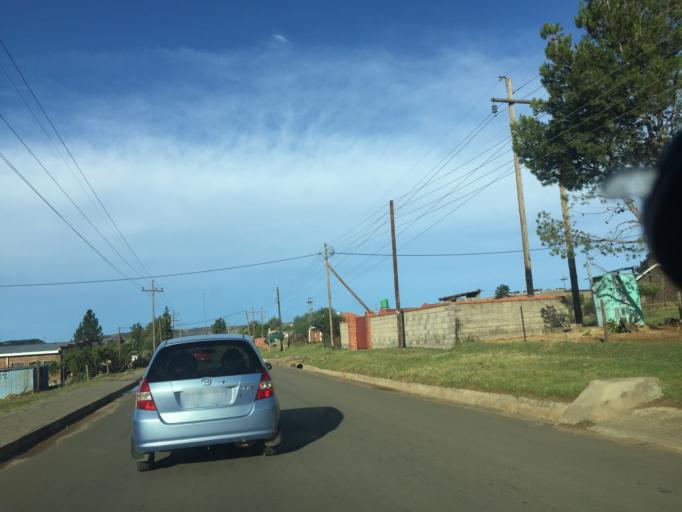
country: LS
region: Maseru
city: Maseru
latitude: -29.2867
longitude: 27.5337
